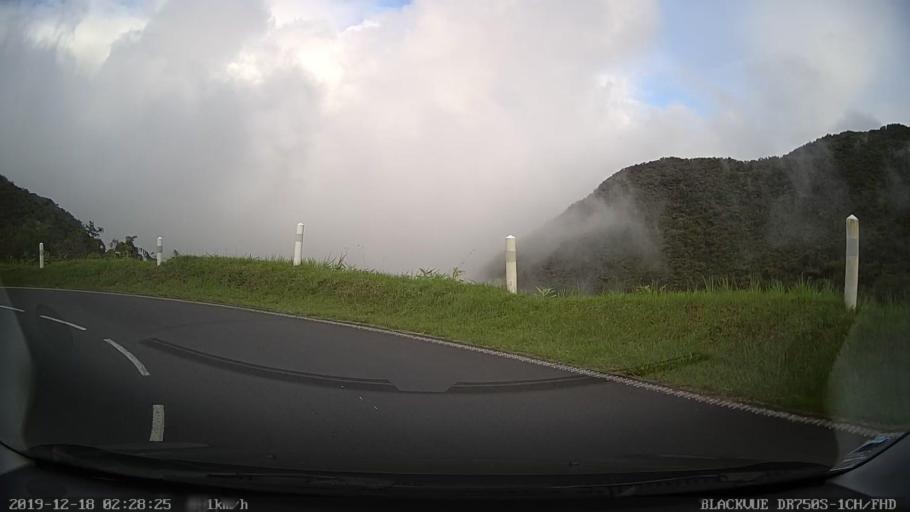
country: RE
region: Reunion
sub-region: Reunion
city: Cilaos
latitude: -21.1590
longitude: 55.5967
